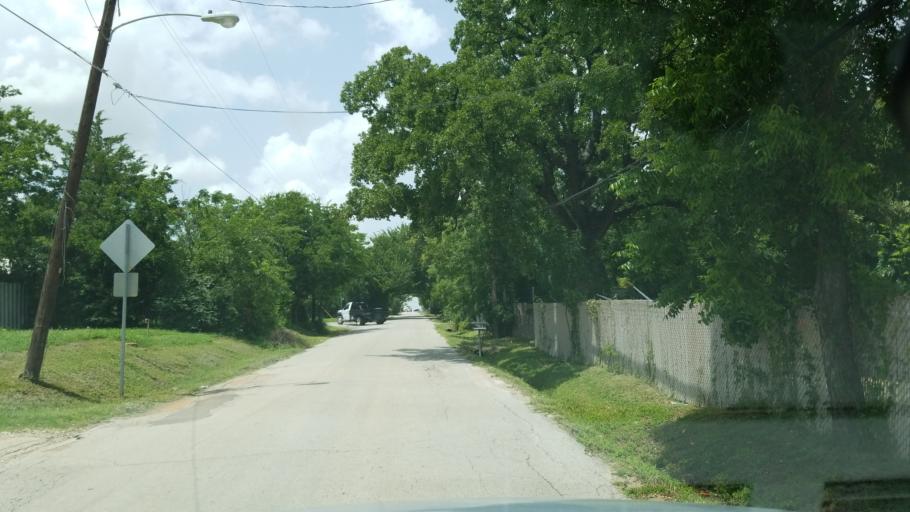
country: US
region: Texas
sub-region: Dallas County
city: Irving
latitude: 32.8268
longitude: -96.9077
